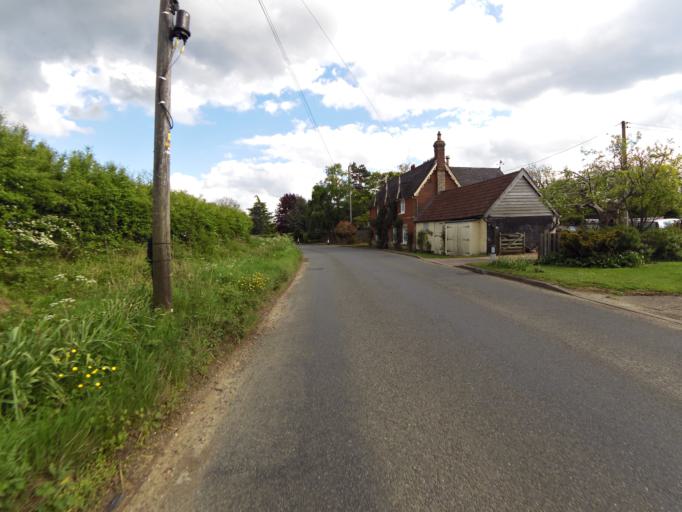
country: GB
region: England
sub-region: Suffolk
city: Elmswell
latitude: 52.2078
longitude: 0.9182
